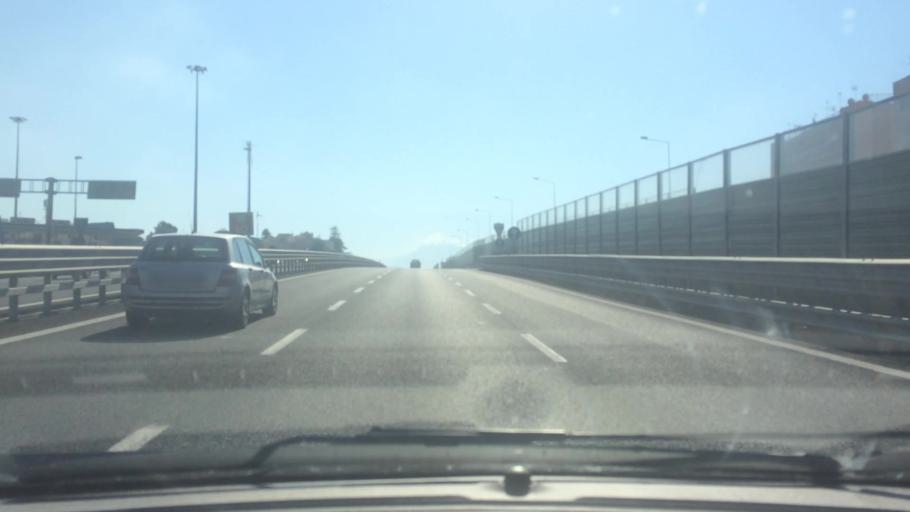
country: IT
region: Campania
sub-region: Provincia di Napoli
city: Ercolano
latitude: 40.8165
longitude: 14.3550
